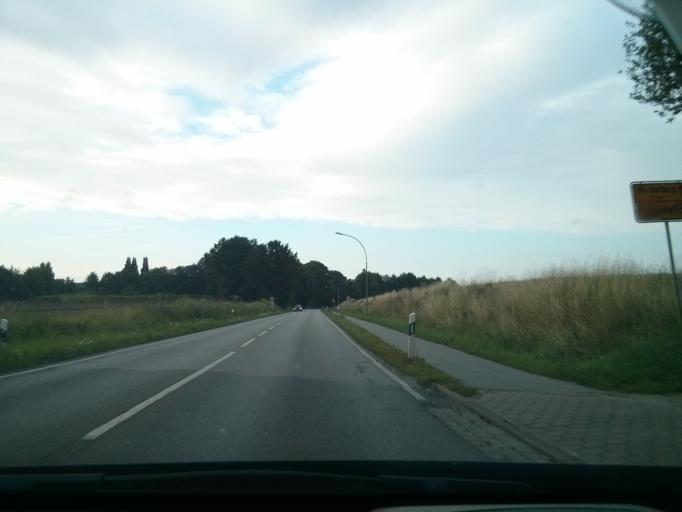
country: DE
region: Lower Saxony
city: Seevetal
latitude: 53.3887
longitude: 9.9741
